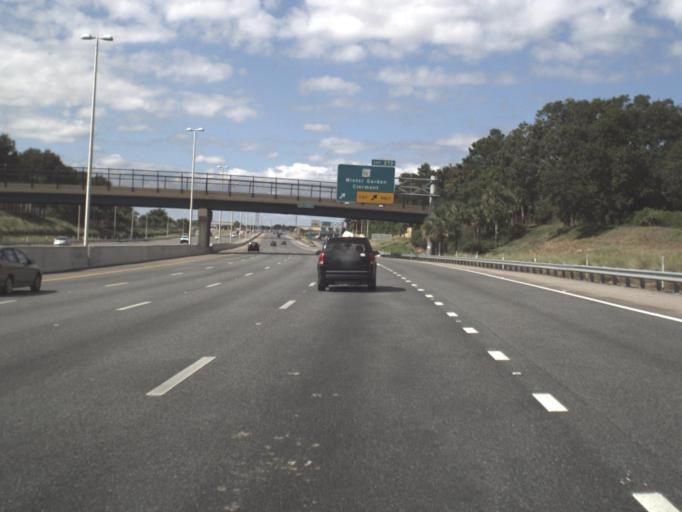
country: US
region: Florida
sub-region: Orange County
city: Oakland
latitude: 28.5484
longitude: -81.6265
